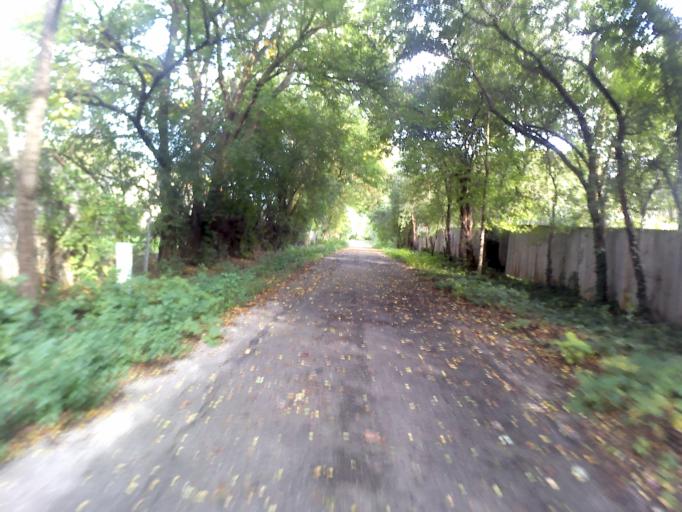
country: US
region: Illinois
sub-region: DuPage County
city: Wheaton
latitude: 41.8391
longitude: -88.1230
